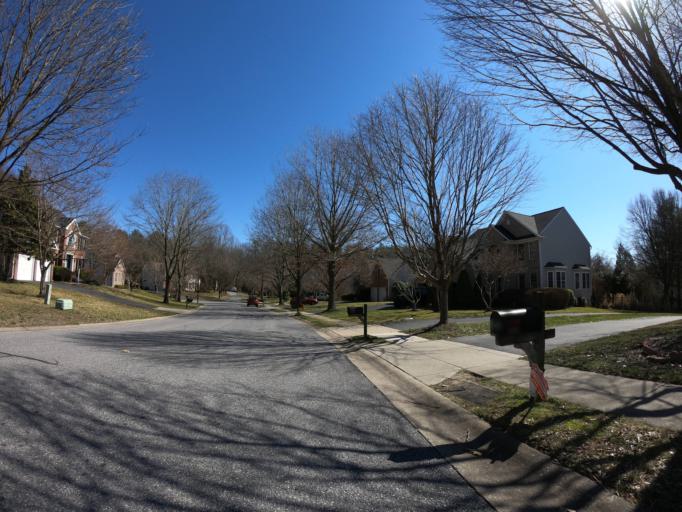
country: US
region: Maryland
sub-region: Howard County
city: Ellicott City
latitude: 39.2803
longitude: -76.7938
